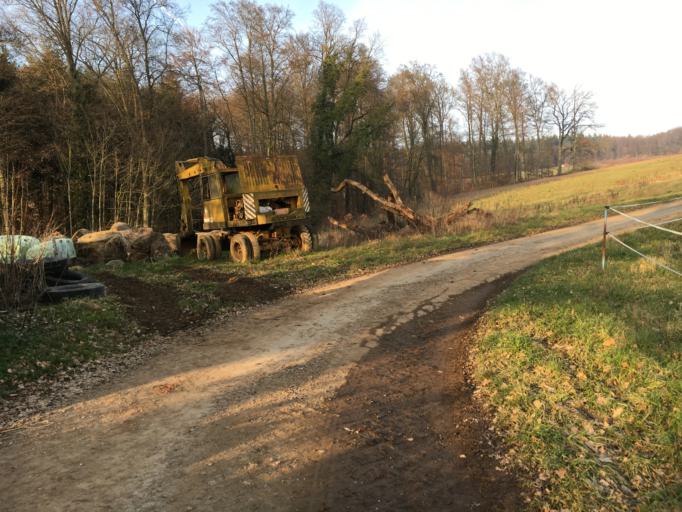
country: DE
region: Baden-Wuerttemberg
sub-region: Karlsruhe Region
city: Huffenhardt
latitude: 49.3206
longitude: 9.0502
